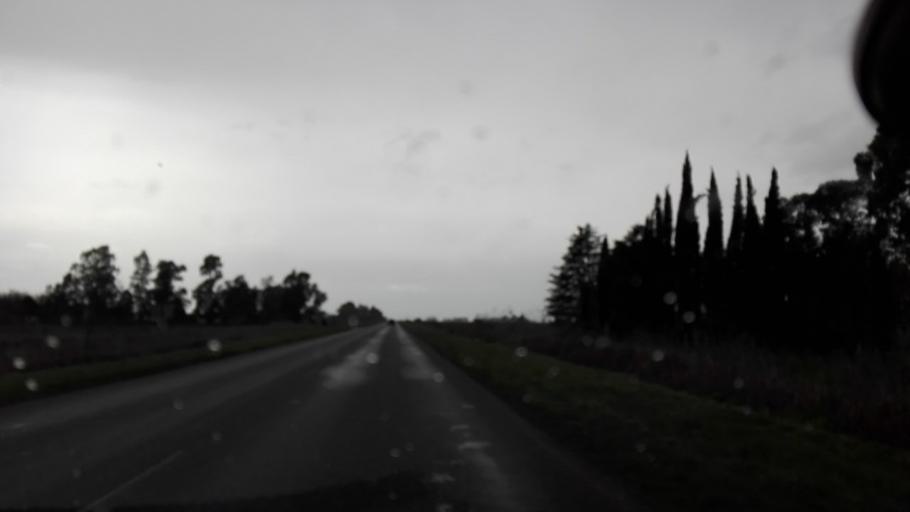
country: AR
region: Buenos Aires
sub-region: Partido de Rauch
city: Rauch
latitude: -36.7560
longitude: -59.0799
